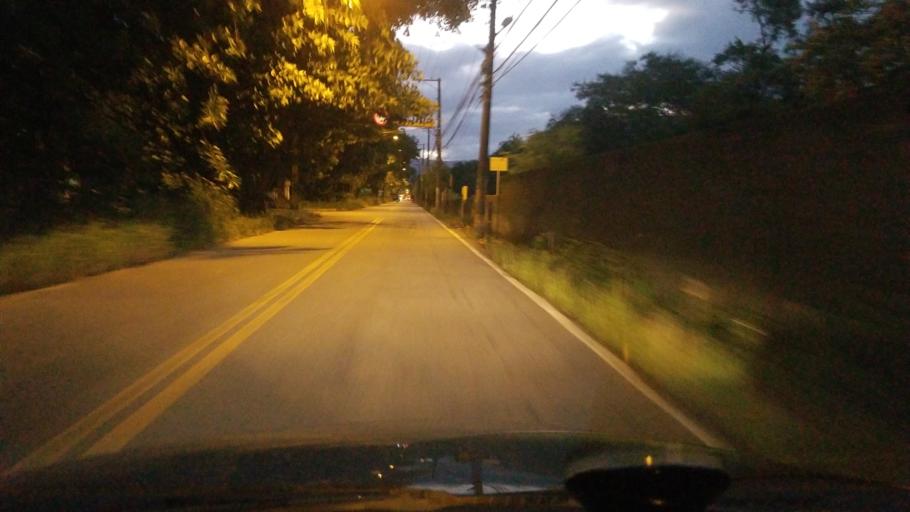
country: BR
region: Sao Paulo
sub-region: Sao Vicente
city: Sao Vicente
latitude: -23.9254
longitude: -46.3847
